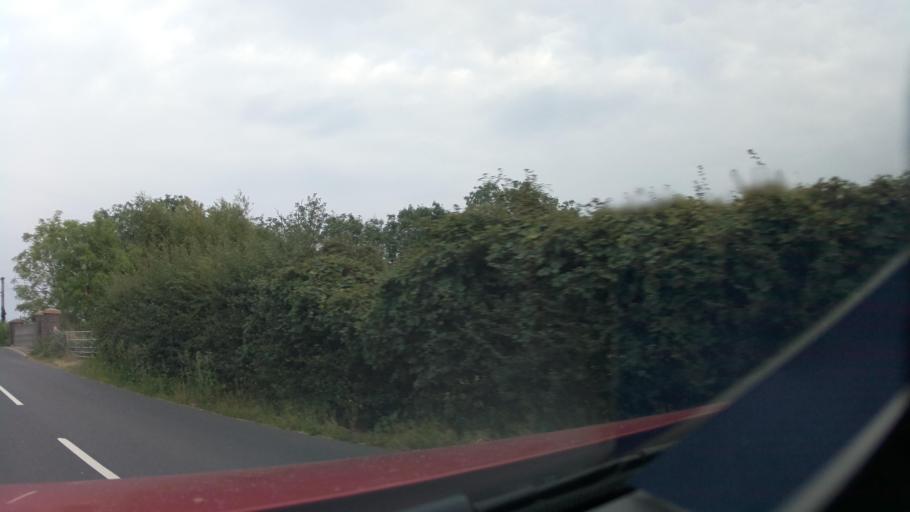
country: GB
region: England
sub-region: Lincolnshire
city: Skellingthorpe
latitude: 53.1340
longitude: -0.6431
